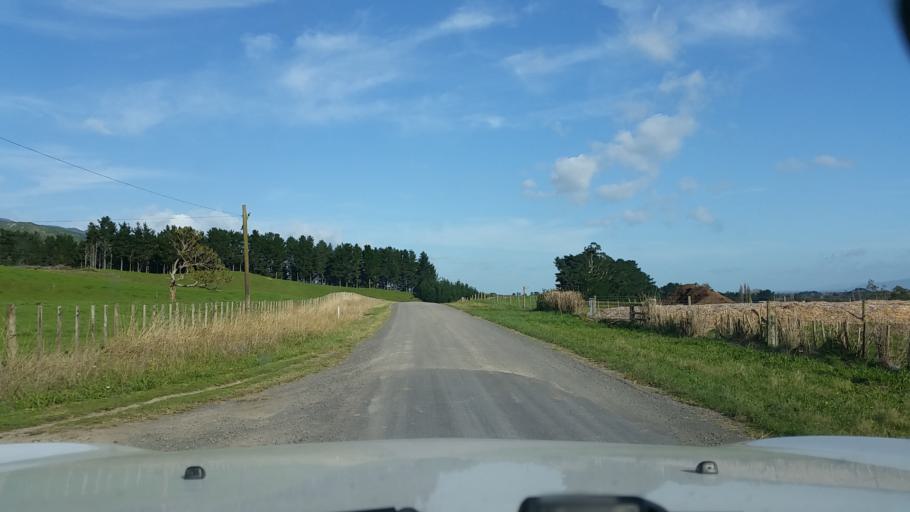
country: NZ
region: Bay of Plenty
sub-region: Western Bay of Plenty District
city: Katikati
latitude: -37.6059
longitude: 175.7970
